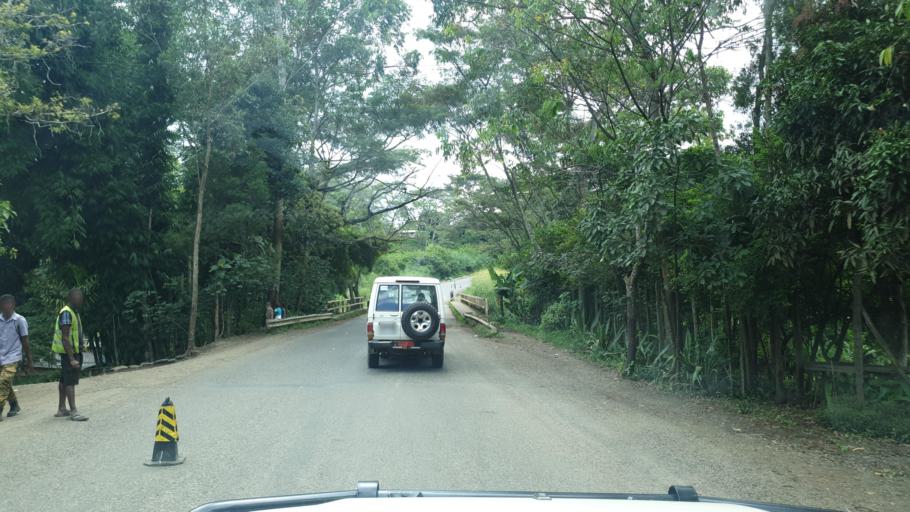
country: PG
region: Eastern Highlands
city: Goroka
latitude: -6.0445
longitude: 145.3747
